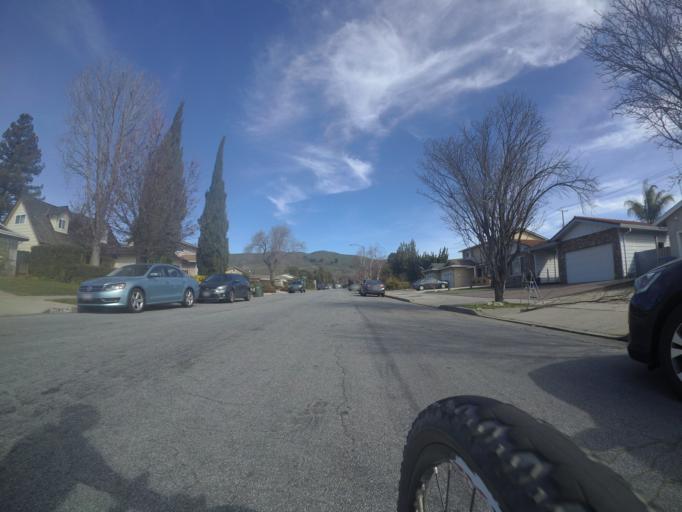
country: US
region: California
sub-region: Santa Clara County
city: Milpitas
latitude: 37.4155
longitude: -121.8656
